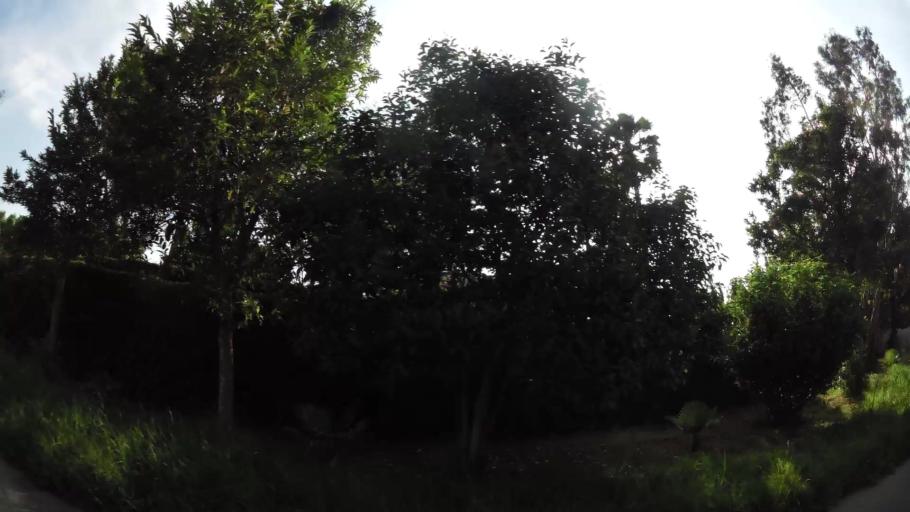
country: MA
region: Rabat-Sale-Zemmour-Zaer
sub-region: Rabat
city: Rabat
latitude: 33.9373
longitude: -6.8042
